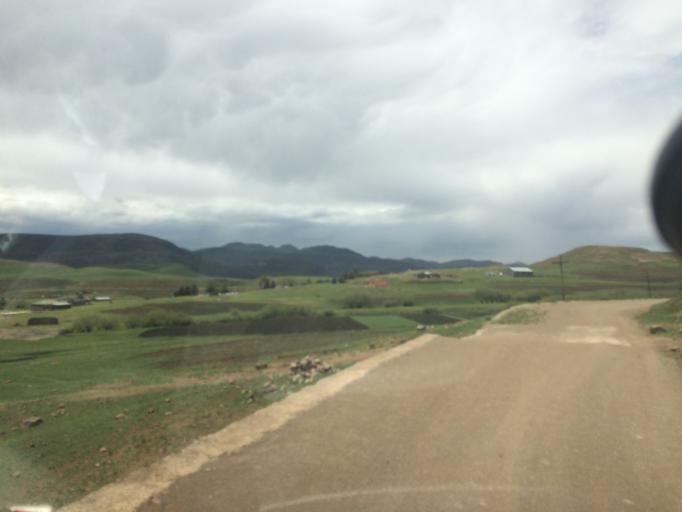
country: LS
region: Maseru
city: Nako
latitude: -29.8608
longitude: 28.0379
